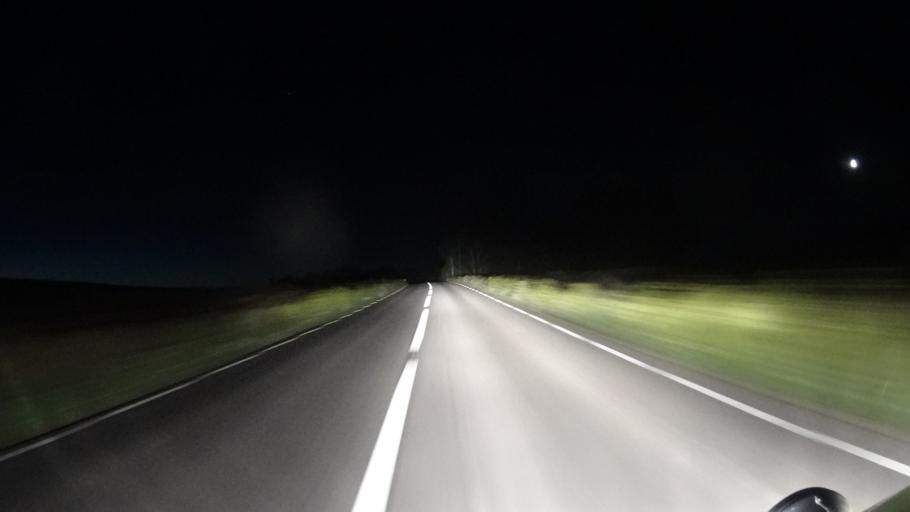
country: SE
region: OEstergoetland
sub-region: Odeshogs Kommun
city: OEdeshoeg
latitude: 58.2430
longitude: 14.7162
